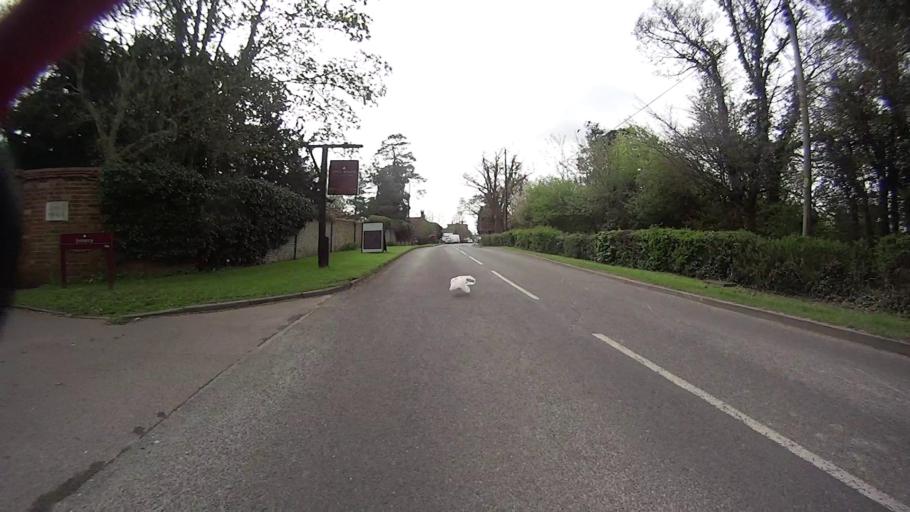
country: GB
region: England
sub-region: Surrey
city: Newdigate
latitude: 51.1236
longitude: -0.2793
